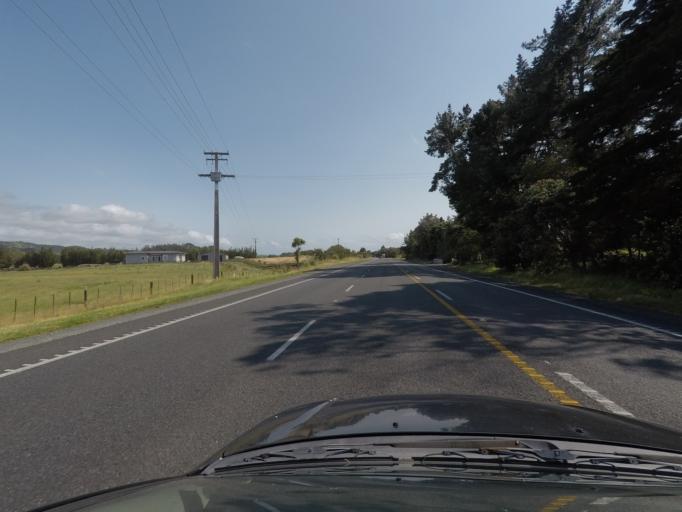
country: NZ
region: Northland
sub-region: Whangarei
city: Ruakaka
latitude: -35.9491
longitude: 174.4541
